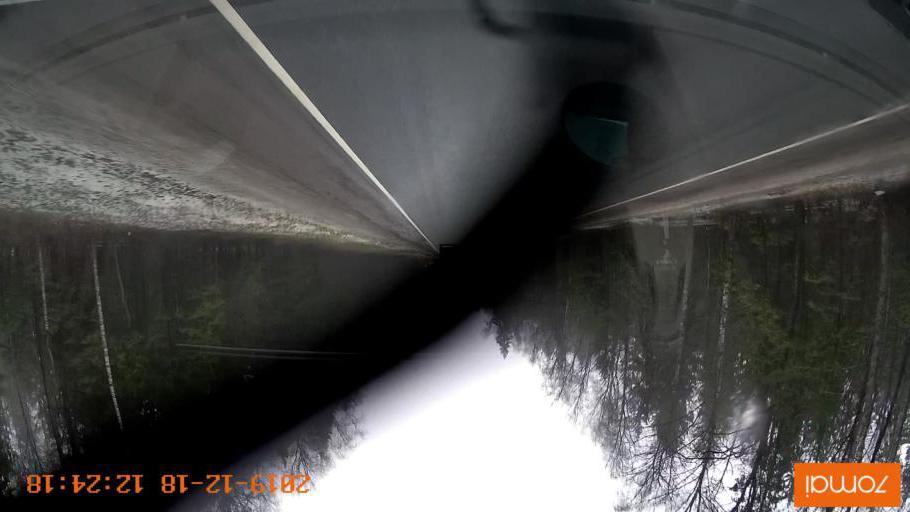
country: RU
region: Moskovskaya
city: Novopetrovskoye
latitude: 56.0228
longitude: 36.5000
